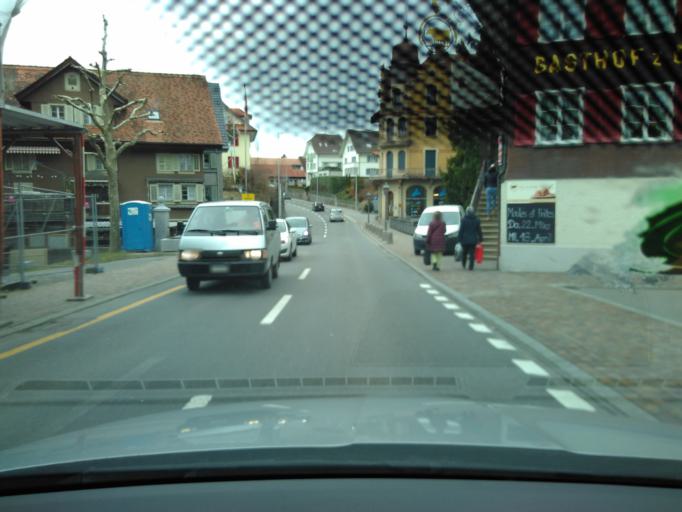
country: CH
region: Lucerne
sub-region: Hochdorf District
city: Emmen
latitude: 47.0943
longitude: 8.2720
